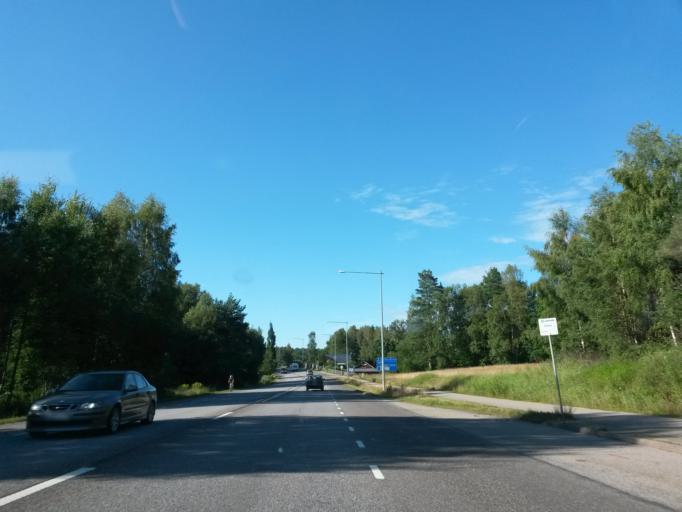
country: SE
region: Vaestra Goetaland
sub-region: Boras Kommun
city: Ganghester
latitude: 57.8095
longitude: 13.0119
